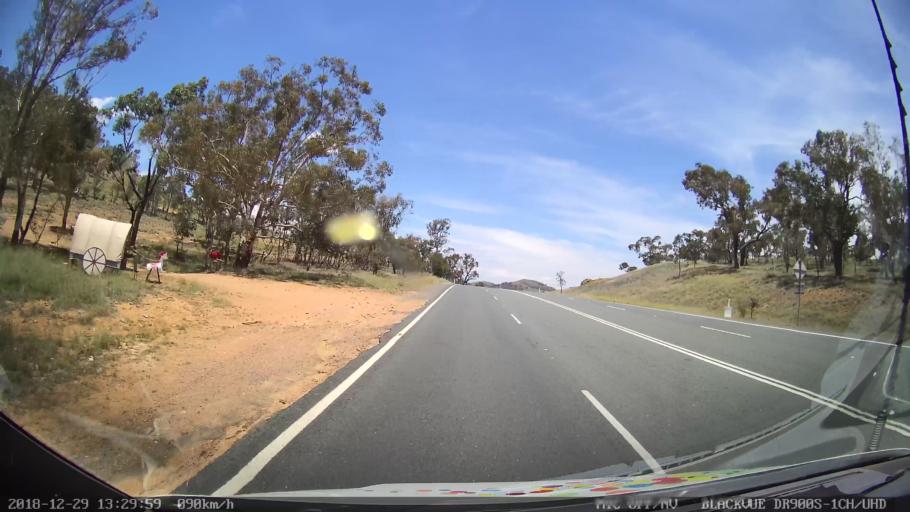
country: AU
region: New South Wales
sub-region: Cooma-Monaro
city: Cooma
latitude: -35.8977
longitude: 149.1613
